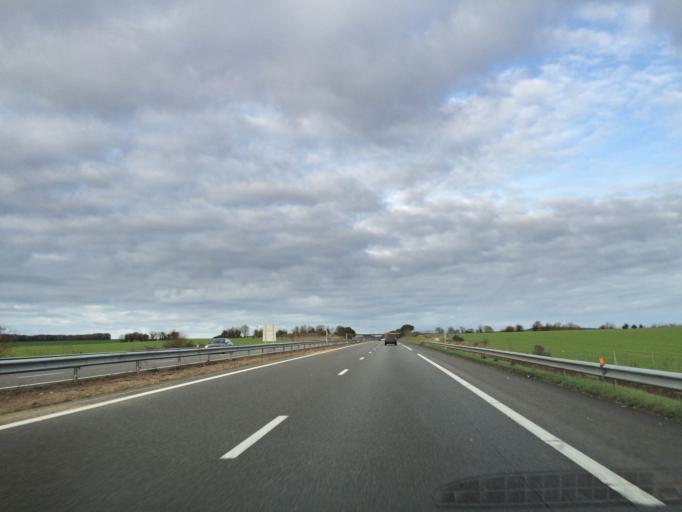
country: FR
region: Poitou-Charentes
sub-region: Departement de la Charente-Maritime
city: Saint-Jean-d'Angely
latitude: 45.9832
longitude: -0.5453
